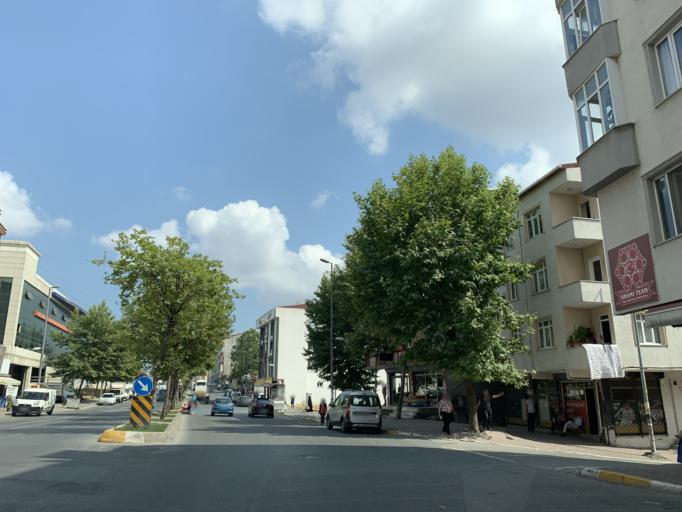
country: TR
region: Istanbul
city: Esenyurt
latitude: 41.0396
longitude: 28.6622
